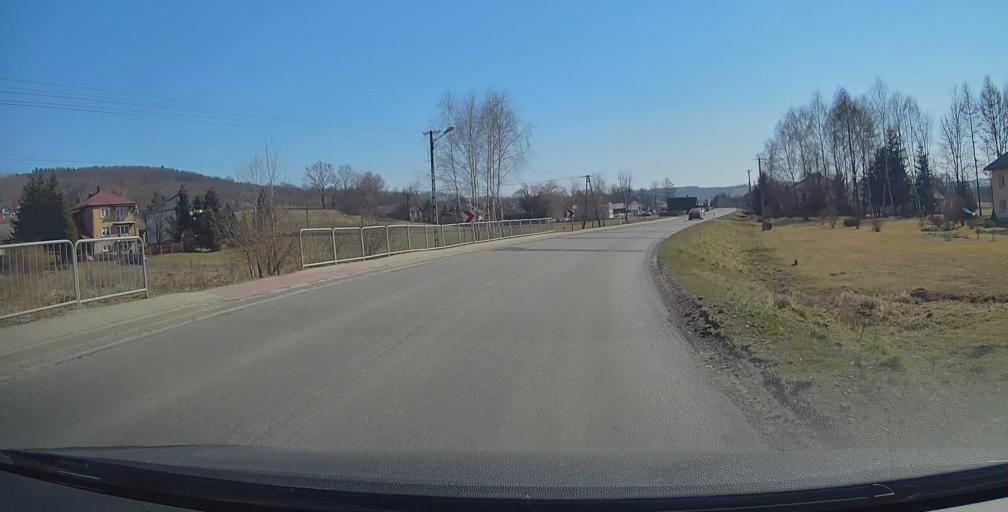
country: PL
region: Subcarpathian Voivodeship
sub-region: Powiat rzeszowski
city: Chmielnik
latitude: 49.9604
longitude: 22.0951
